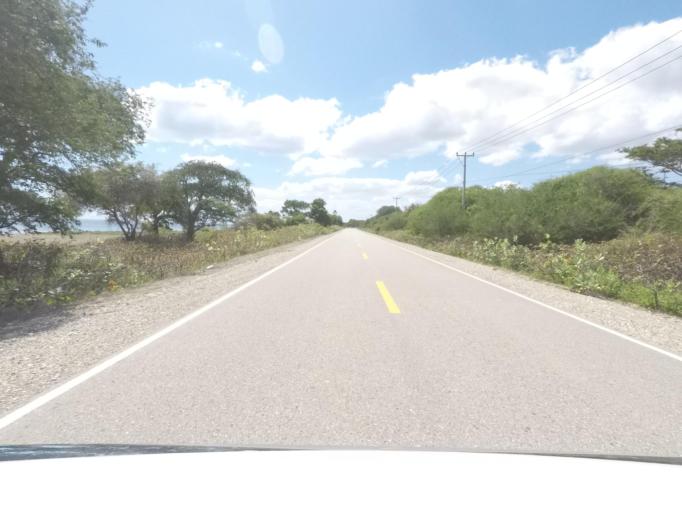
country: TL
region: Baucau
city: Baucau
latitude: -8.4275
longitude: 126.6921
